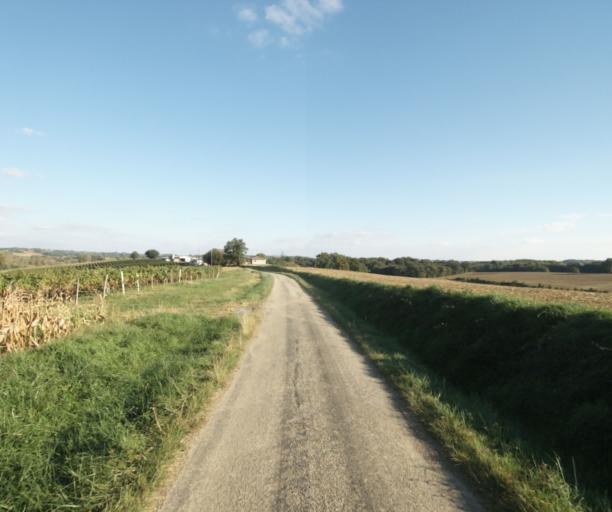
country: FR
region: Midi-Pyrenees
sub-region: Departement du Gers
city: Eauze
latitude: 43.7648
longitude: 0.1420
